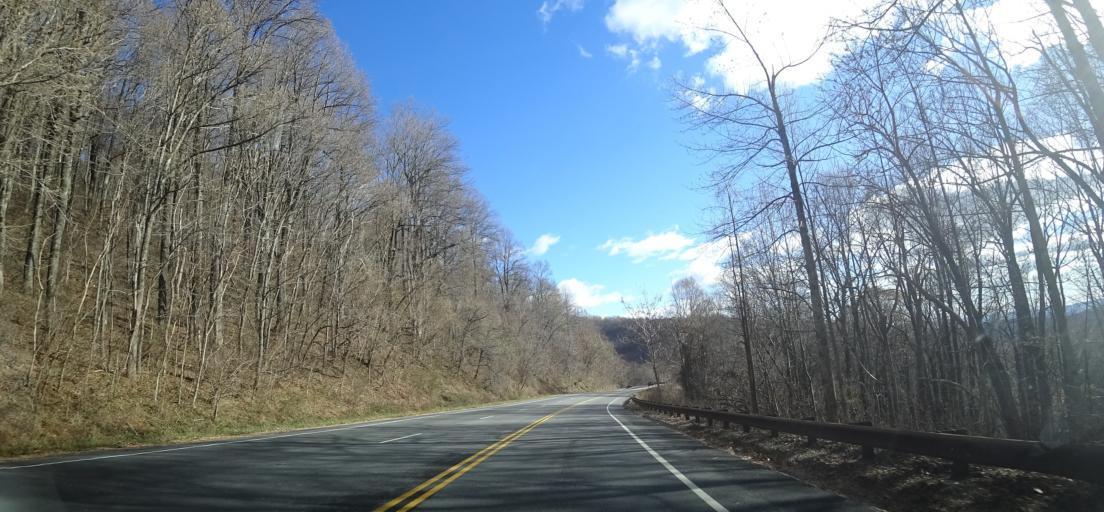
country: US
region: Virginia
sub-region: Rockingham County
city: Elkton
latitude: 38.3554
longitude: -78.5423
